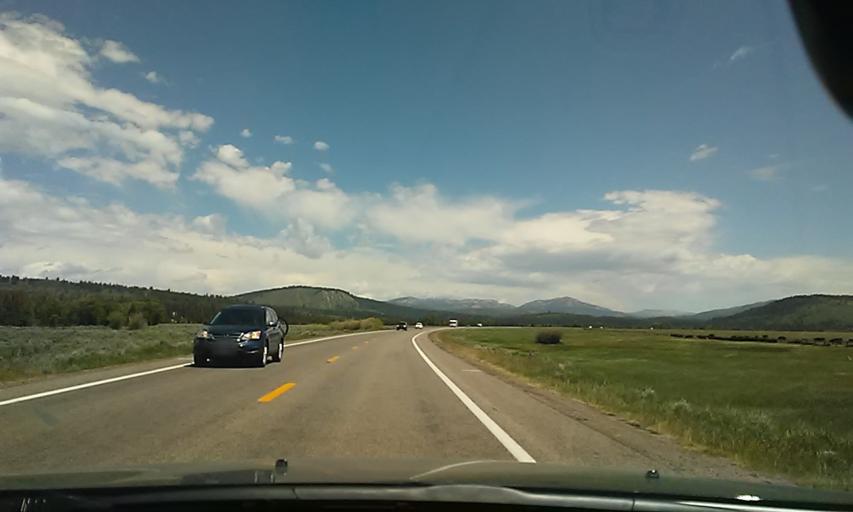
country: US
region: Wyoming
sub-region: Teton County
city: Jackson
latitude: 43.8138
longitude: -110.5261
